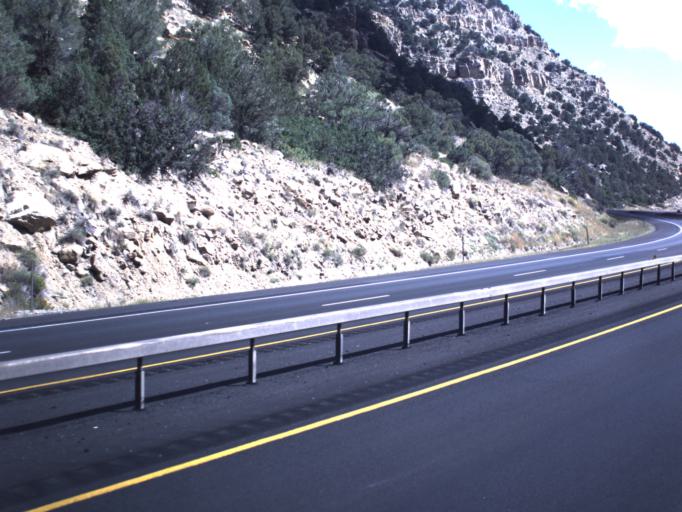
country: US
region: Utah
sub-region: Sevier County
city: Salina
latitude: 38.8823
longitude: -111.5936
